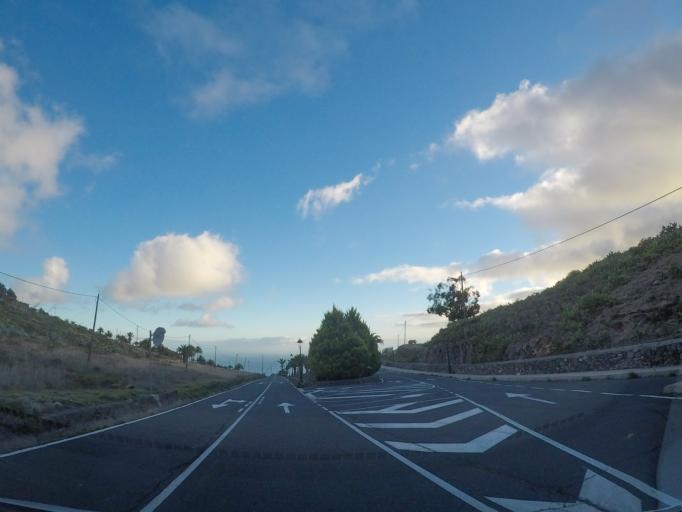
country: ES
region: Canary Islands
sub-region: Provincia de Santa Cruz de Tenerife
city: Alajero
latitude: 28.0696
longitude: -17.2389
